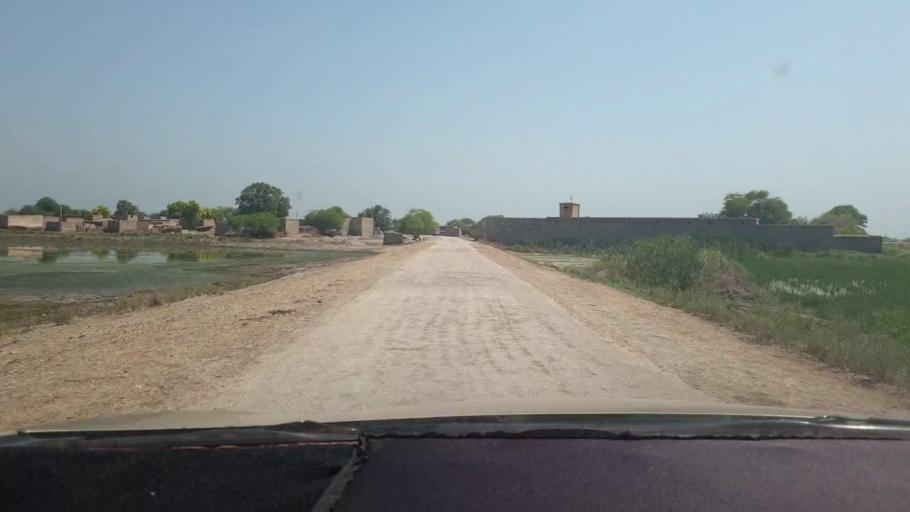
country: PK
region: Sindh
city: Miro Khan
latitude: 27.6719
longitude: 68.0968
